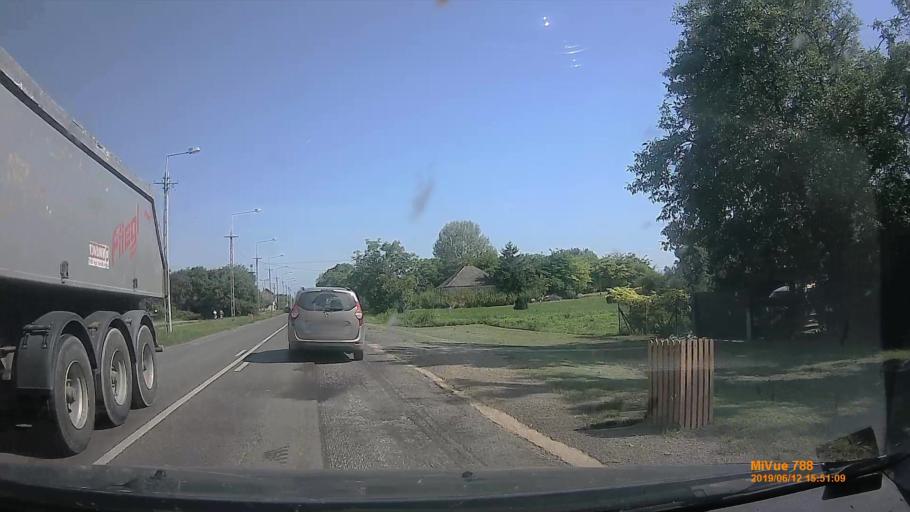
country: HU
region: Csongrad
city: Apatfalva
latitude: 46.1825
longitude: 20.5699
